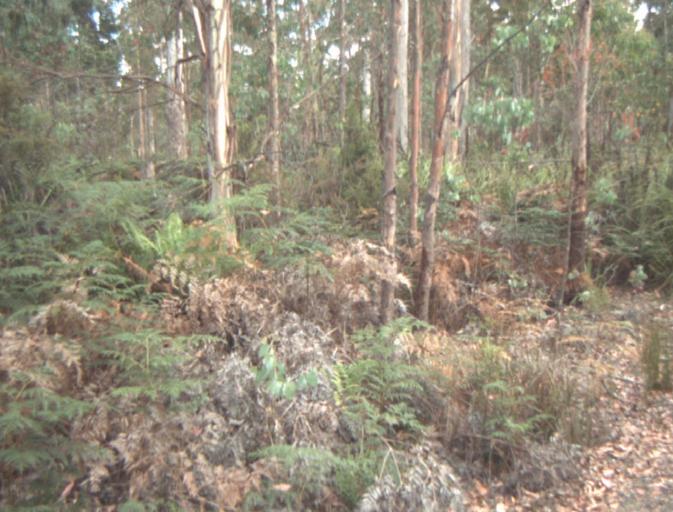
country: AU
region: Tasmania
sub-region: Launceston
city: Mayfield
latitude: -41.2927
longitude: 147.2396
